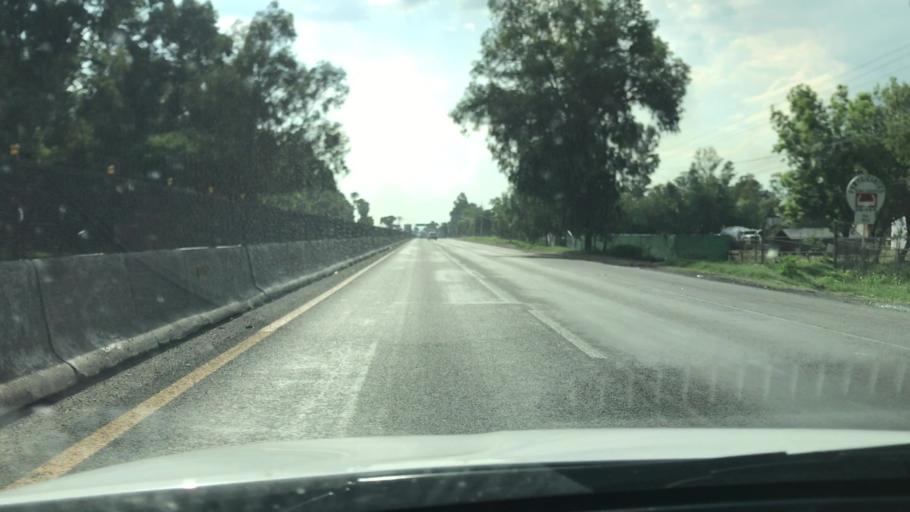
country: MX
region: Guanajuato
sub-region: Salamanca
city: El Divisador
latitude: 20.5551
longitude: -101.1562
